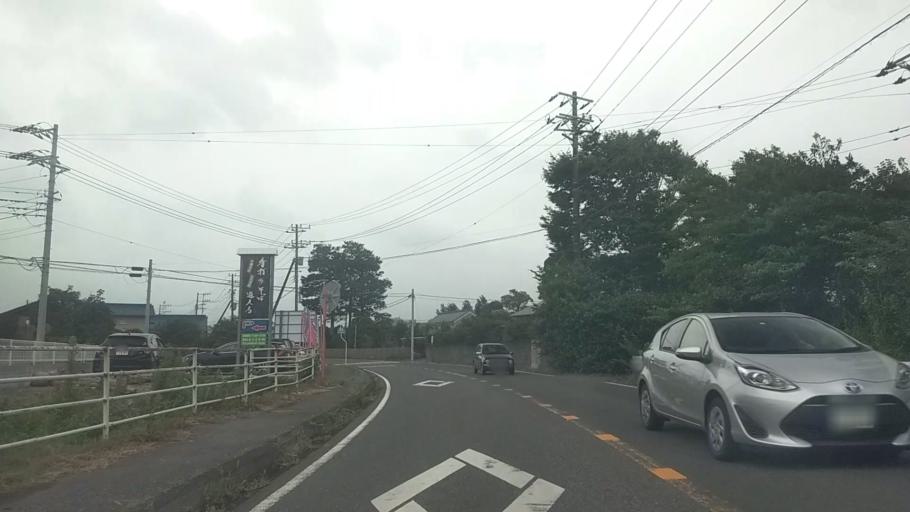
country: JP
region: Chiba
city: Kimitsu
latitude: 35.2169
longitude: 139.8921
